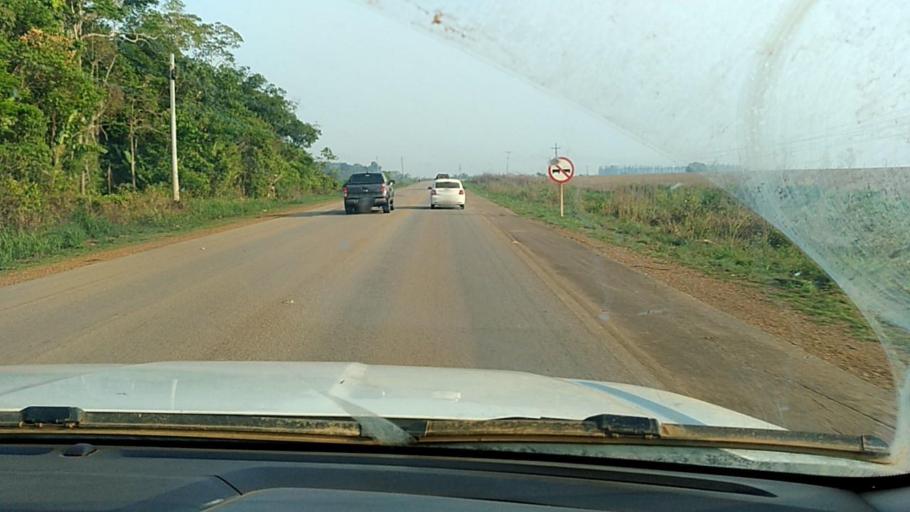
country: BR
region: Rondonia
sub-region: Porto Velho
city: Porto Velho
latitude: -8.6980
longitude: -63.9925
